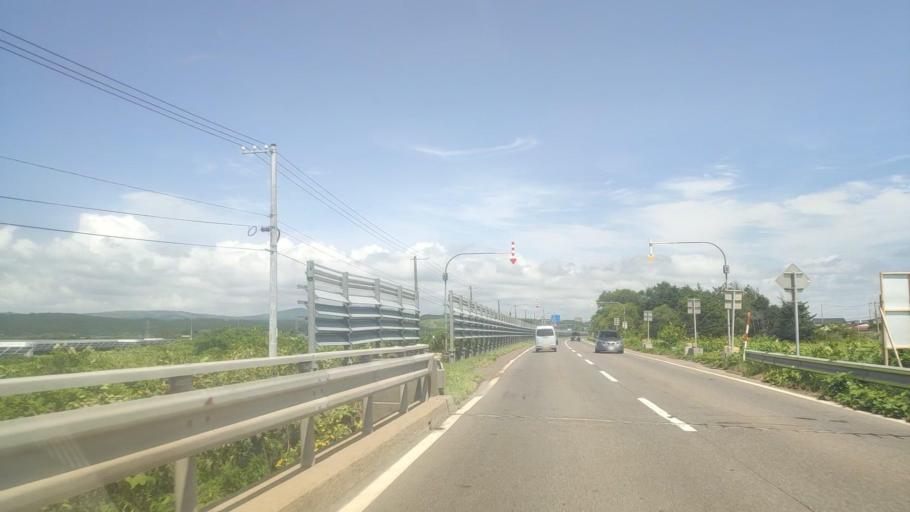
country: JP
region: Hokkaido
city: Nanae
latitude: 42.3034
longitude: 140.2721
